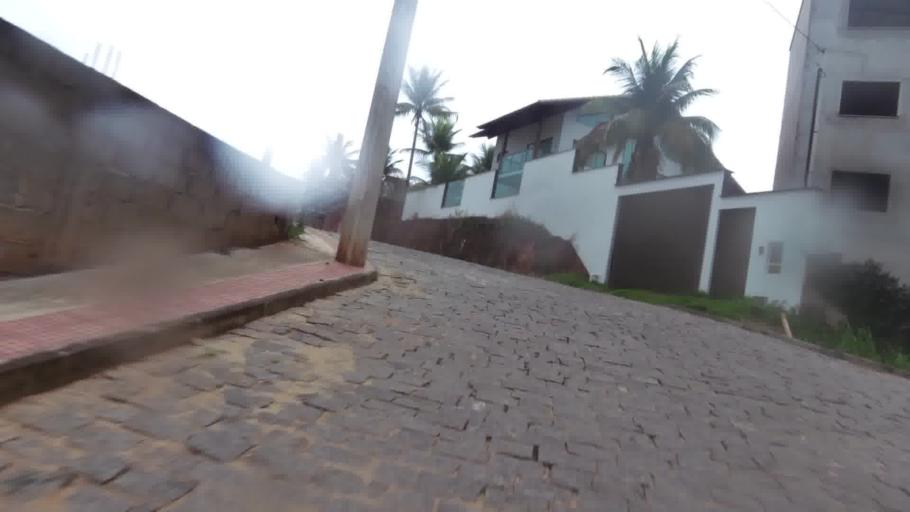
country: BR
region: Espirito Santo
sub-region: Alfredo Chaves
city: Alfredo Chaves
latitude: -20.6397
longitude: -40.7470
